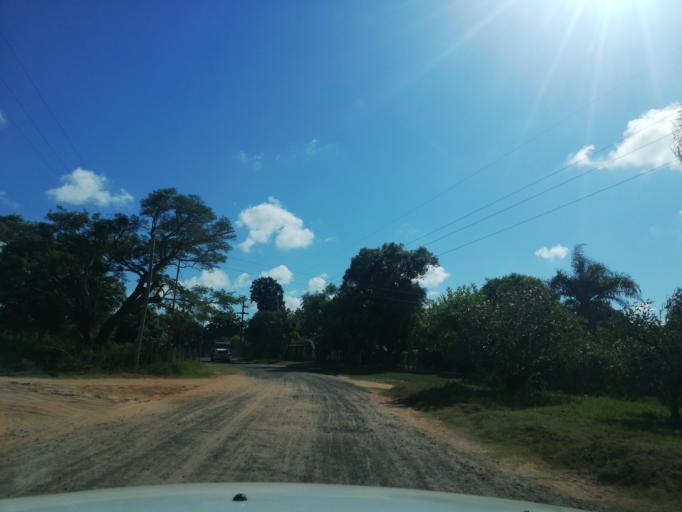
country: AR
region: Corrientes
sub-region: Departamento de San Miguel
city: San Miguel
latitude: -27.9908
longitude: -57.5887
